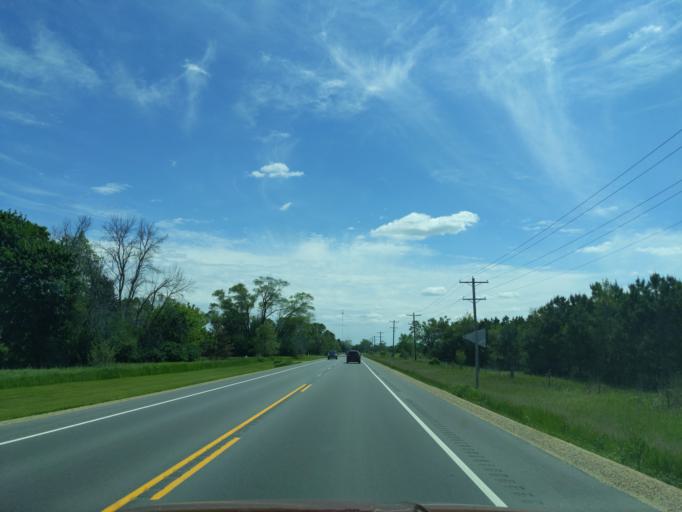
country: US
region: Wisconsin
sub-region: Columbia County
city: Pardeeville
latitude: 43.5192
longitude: -89.3058
